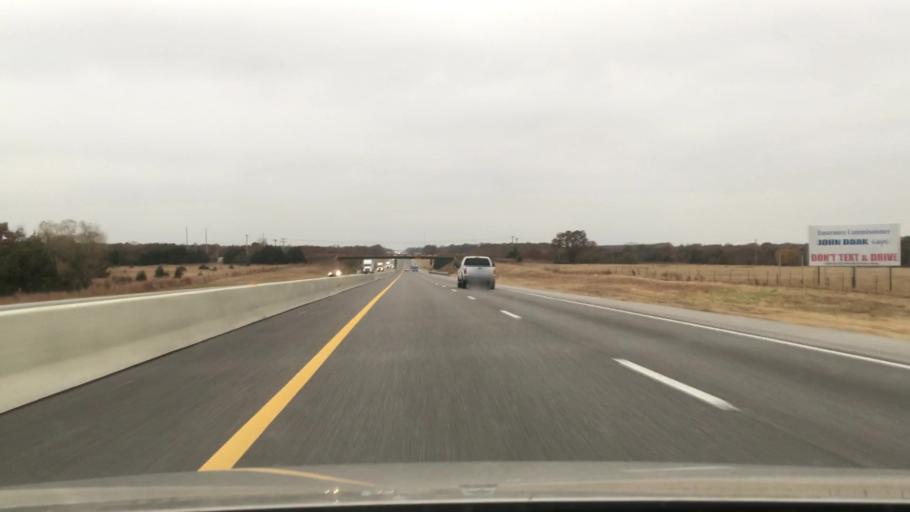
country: US
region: Oklahoma
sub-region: Lincoln County
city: Chandler
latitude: 35.7279
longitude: -96.8373
